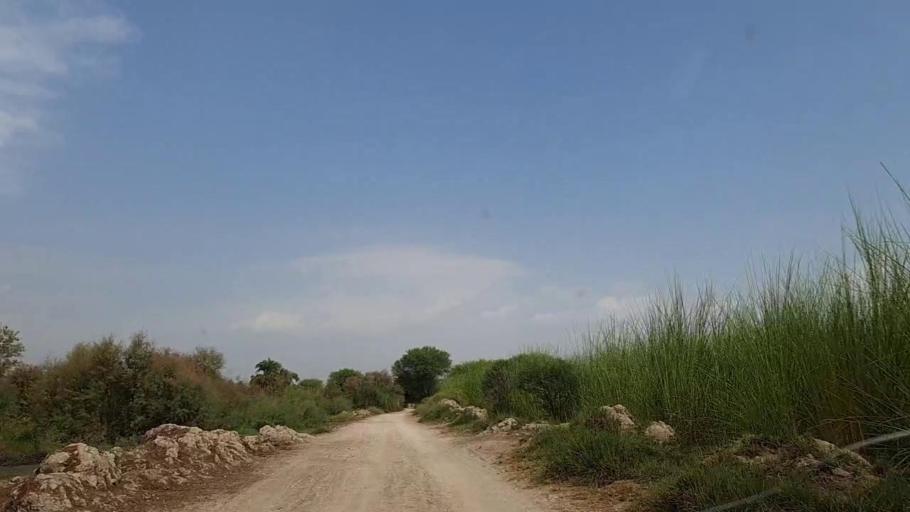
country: PK
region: Sindh
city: Khanpur
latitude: 27.8344
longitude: 69.5012
